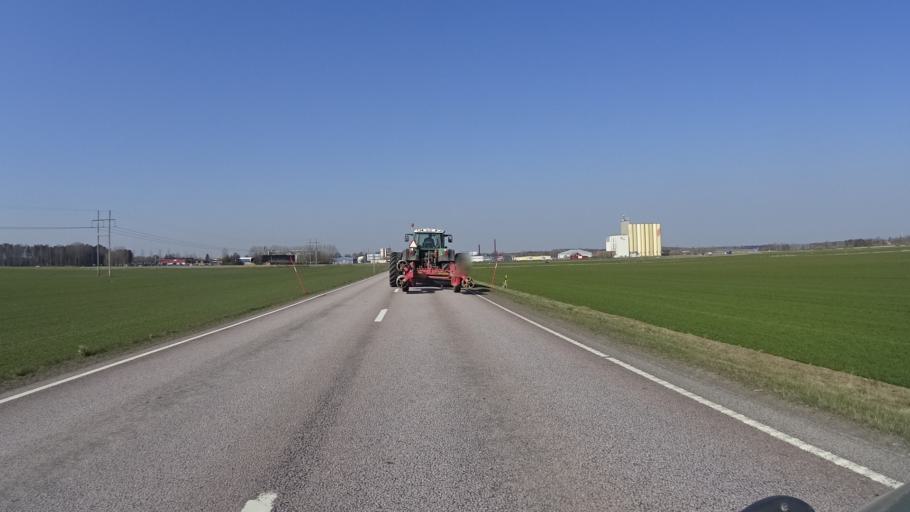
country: SE
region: OEstergoetland
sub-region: Mjolby Kommun
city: Mjolby
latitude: 58.3920
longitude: 15.1128
